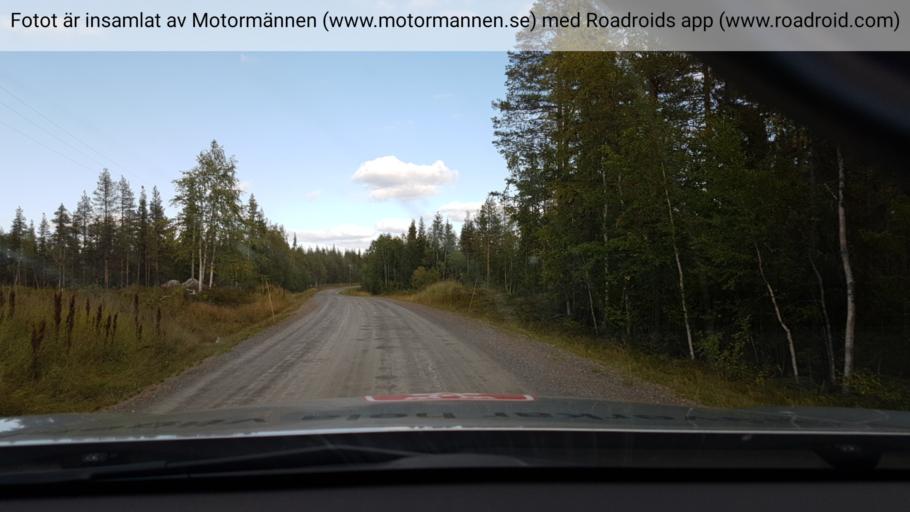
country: SE
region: Vaesterbotten
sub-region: Sorsele Kommun
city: Sorsele
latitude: 65.4557
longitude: 17.7287
